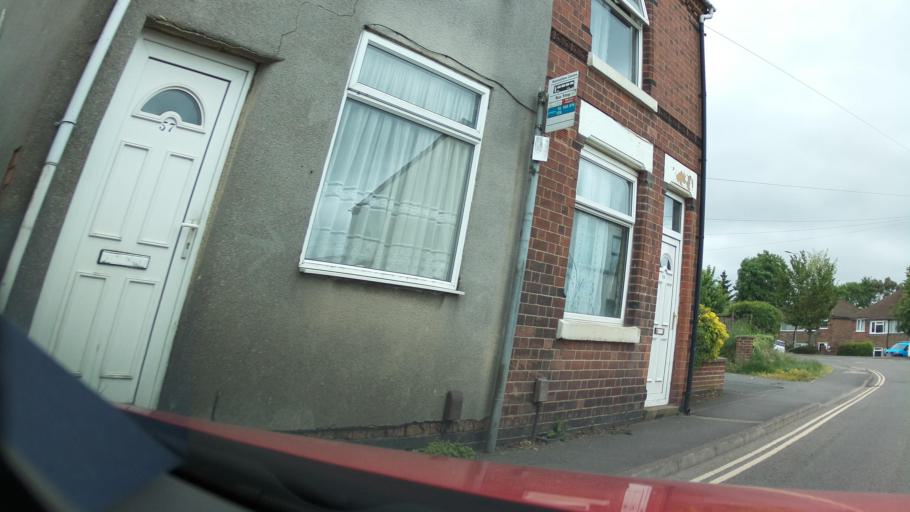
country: GB
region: England
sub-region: Leicestershire
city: Coalville
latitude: 52.7383
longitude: -1.3571
